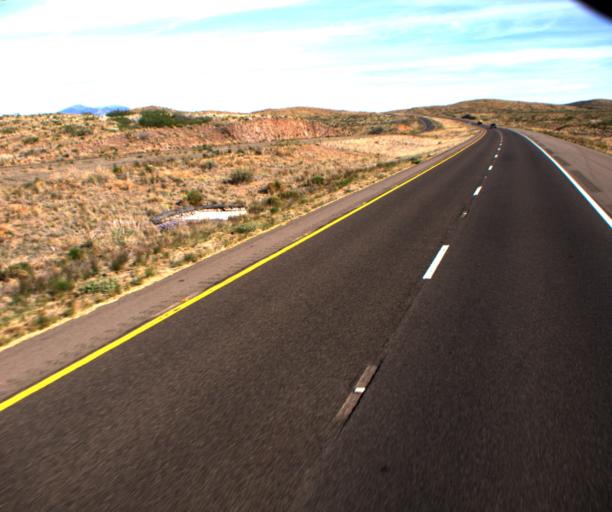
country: US
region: Arizona
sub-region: Cochise County
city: Willcox
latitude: 32.4455
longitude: -109.6634
